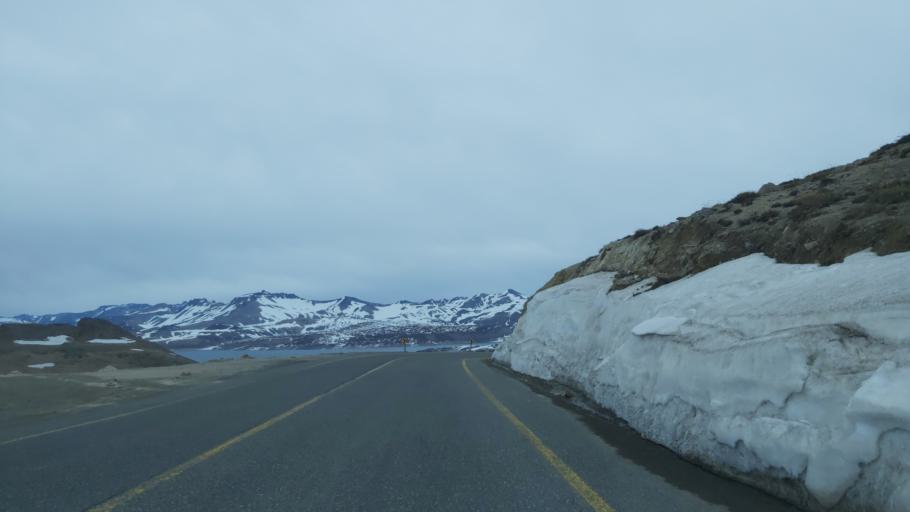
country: CL
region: Maule
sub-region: Provincia de Linares
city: Colbun
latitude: -36.0196
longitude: -70.4990
